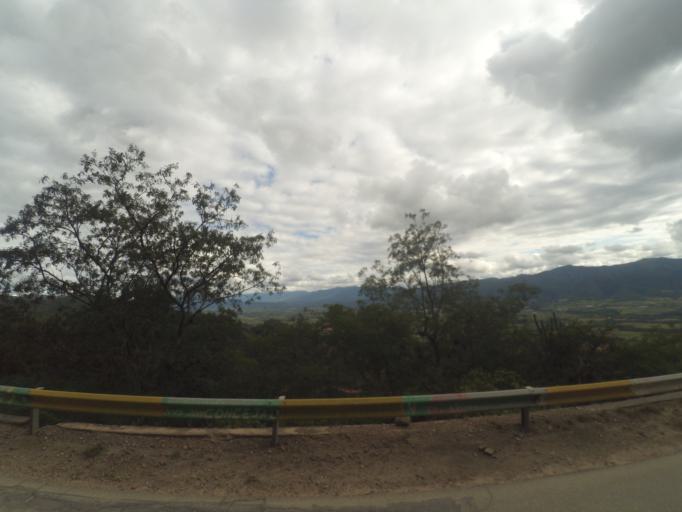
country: BO
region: Santa Cruz
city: Samaipata
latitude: -18.1718
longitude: -63.8812
